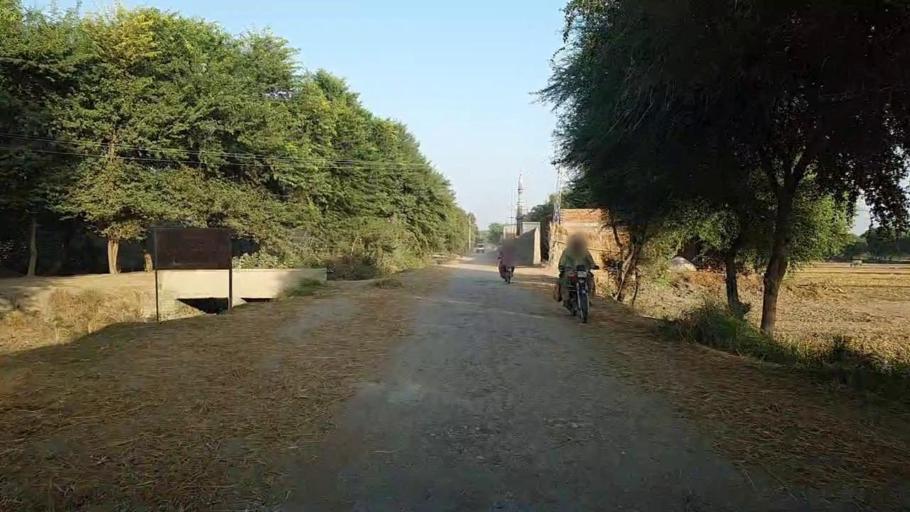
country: PK
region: Sindh
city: Kashmor
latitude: 28.4285
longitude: 69.4619
